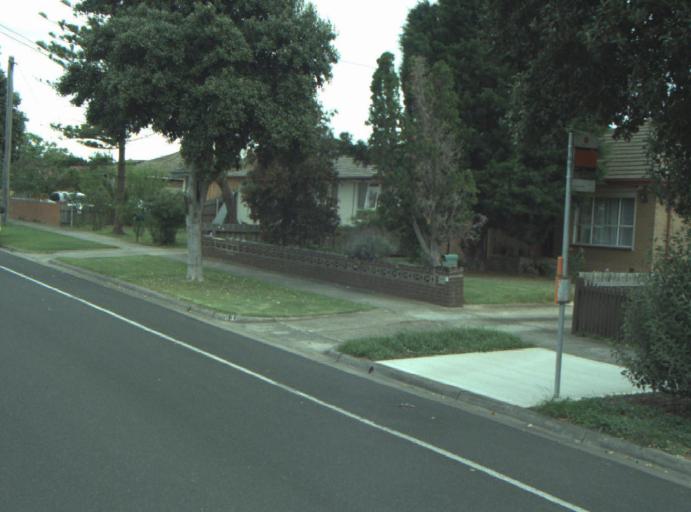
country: AU
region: Victoria
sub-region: Greater Geelong
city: Bell Park
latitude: -38.0684
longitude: 144.3672
